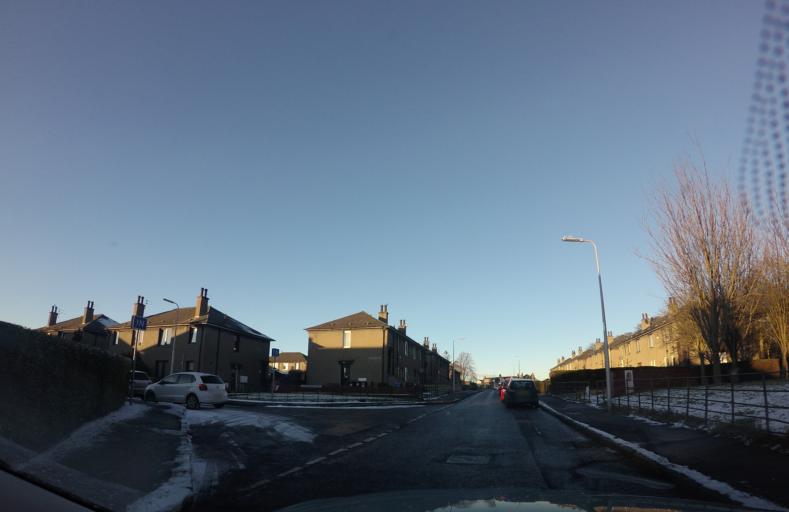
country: GB
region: Scotland
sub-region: Dundee City
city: Dundee
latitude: 56.4769
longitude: -2.9898
